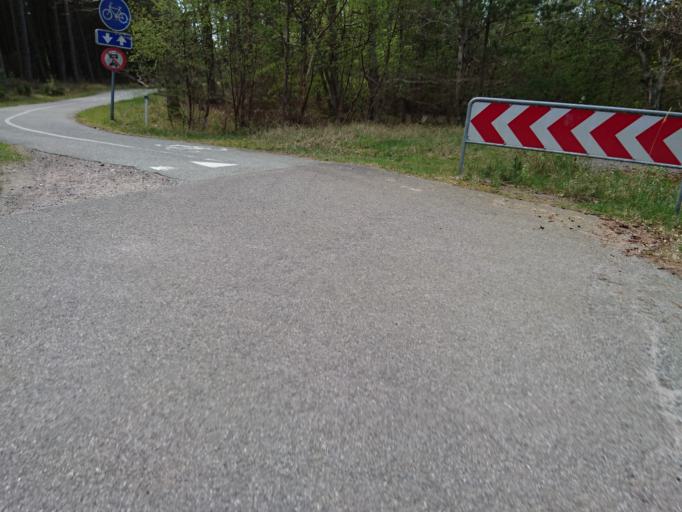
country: DK
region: North Denmark
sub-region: Frederikshavn Kommune
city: Skagen
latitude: 57.6506
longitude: 10.4609
